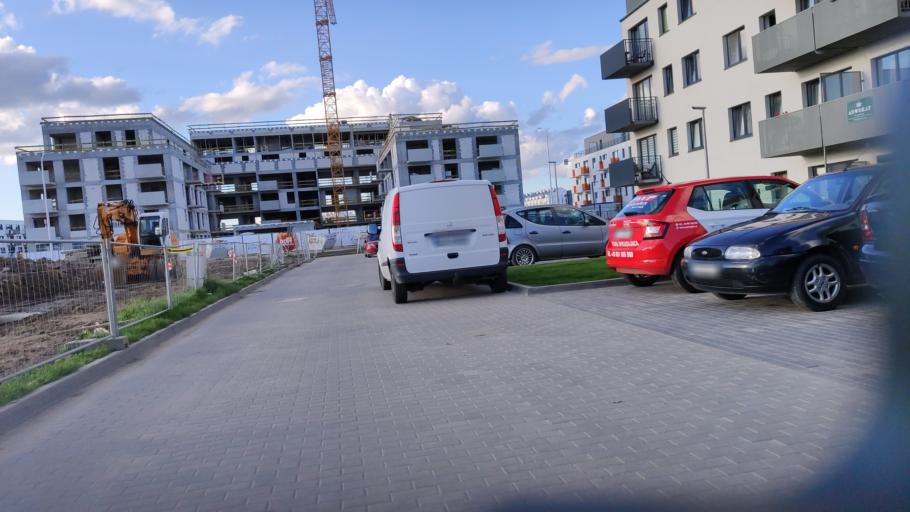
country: PL
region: Lower Silesian Voivodeship
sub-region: Powiat wroclawski
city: Zerniki Wroclawskie
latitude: 51.0552
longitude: 17.0524
